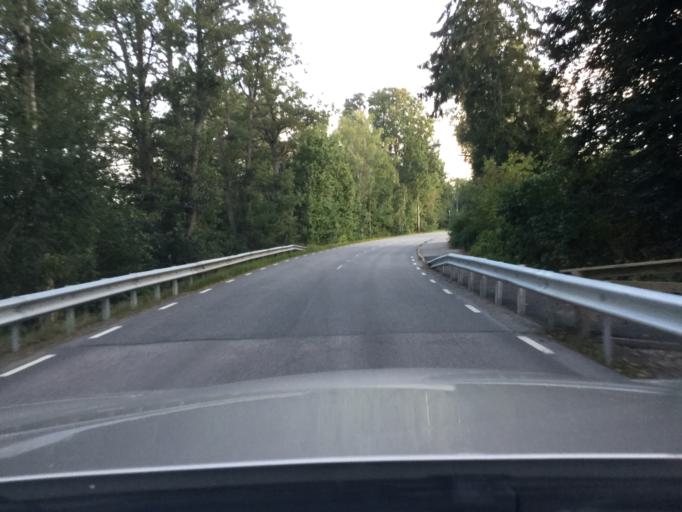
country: SE
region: Kronoberg
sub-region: Almhults Kommun
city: AElmhult
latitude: 56.6405
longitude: 14.2224
